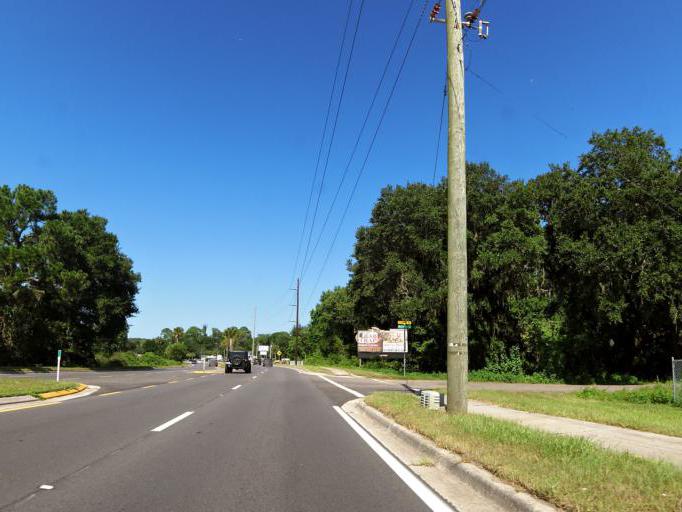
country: US
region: Florida
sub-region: Nassau County
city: Fernandina Beach
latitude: 30.6324
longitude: -81.4643
